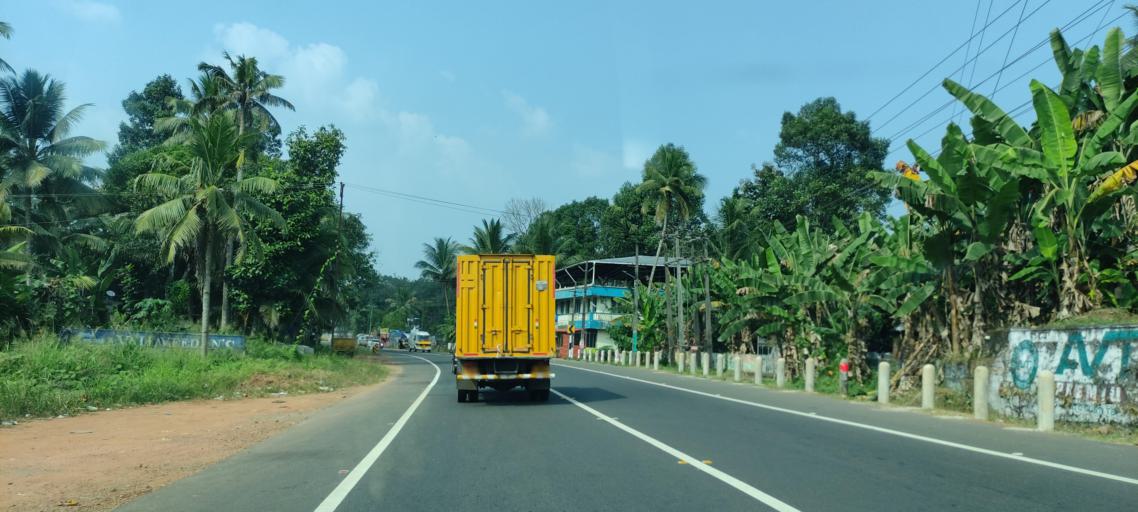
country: IN
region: Kerala
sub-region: Alappuzha
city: Chengannur
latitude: 9.2784
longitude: 76.6558
